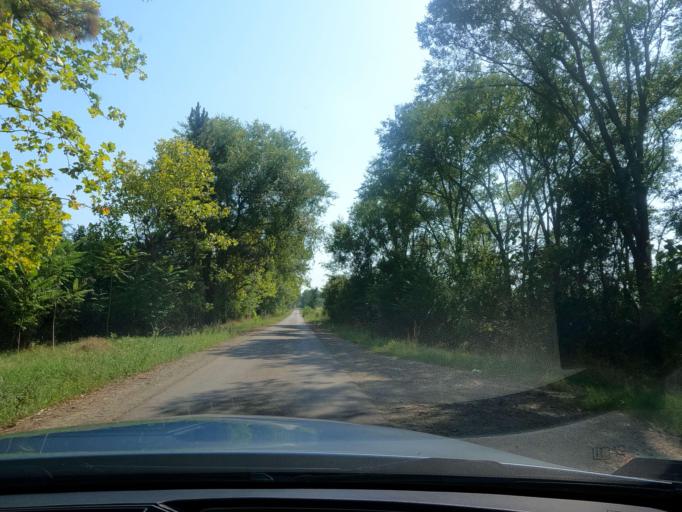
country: RS
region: Autonomna Pokrajina Vojvodina
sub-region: Juznobacki Okrug
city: Becej
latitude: 45.6635
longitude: 19.9075
